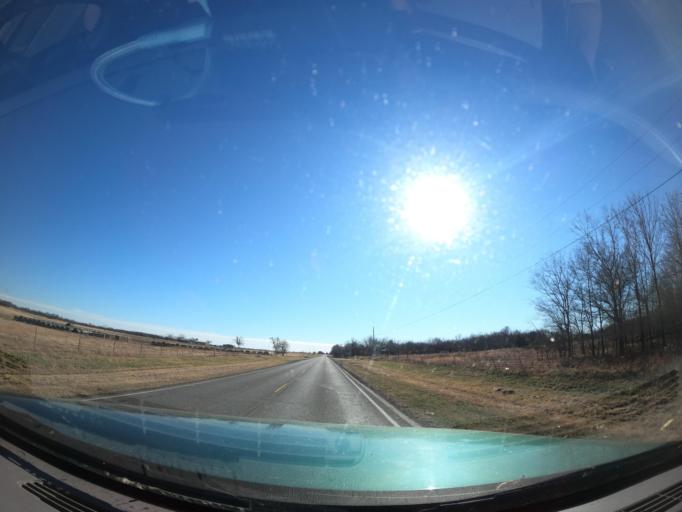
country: US
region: Oklahoma
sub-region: Muskogee County
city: Haskell
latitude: 35.6791
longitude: -95.6422
